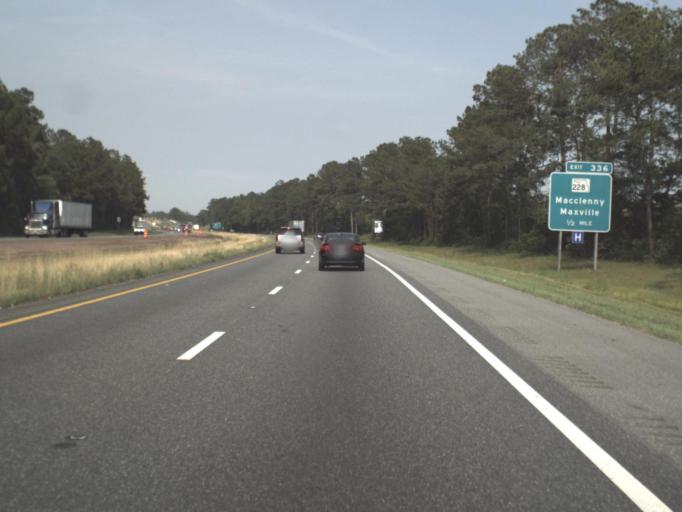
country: US
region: Florida
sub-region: Baker County
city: Macclenny
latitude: 30.2588
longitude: -82.1150
